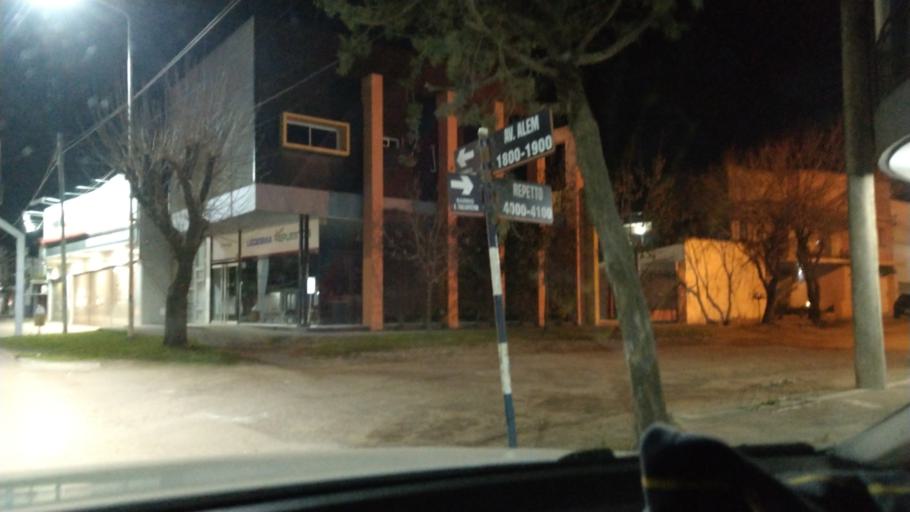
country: AR
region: Entre Rios
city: Chajari
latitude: -30.7618
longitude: -57.9960
